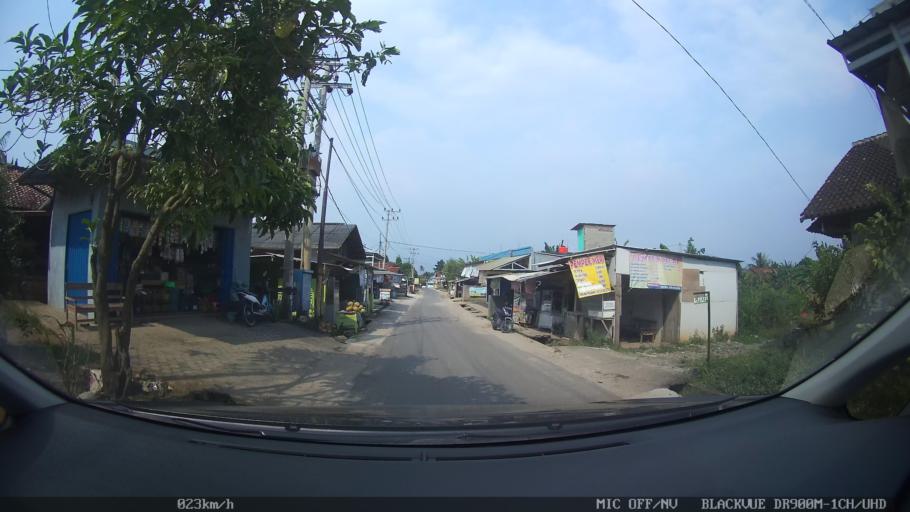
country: ID
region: Lampung
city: Natar
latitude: -5.3467
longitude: 105.2229
